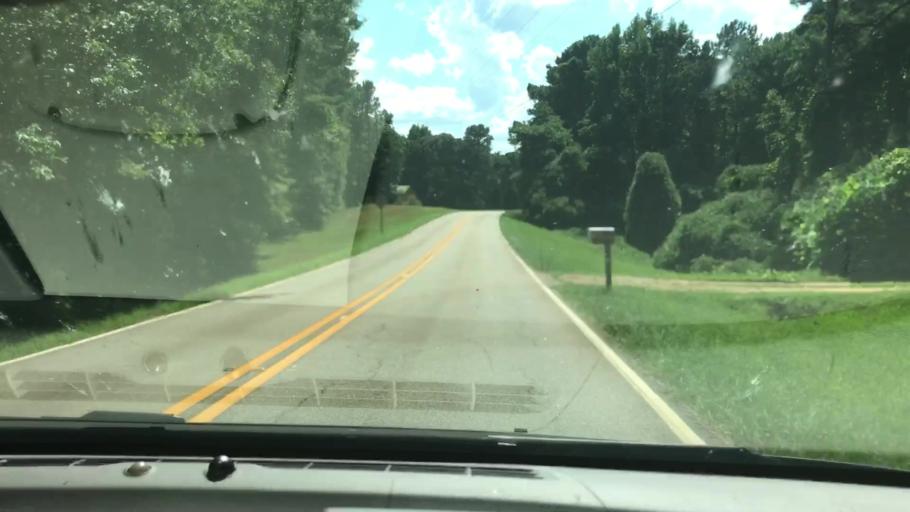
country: US
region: Georgia
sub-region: Troup County
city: La Grange
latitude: 33.1279
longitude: -85.1282
